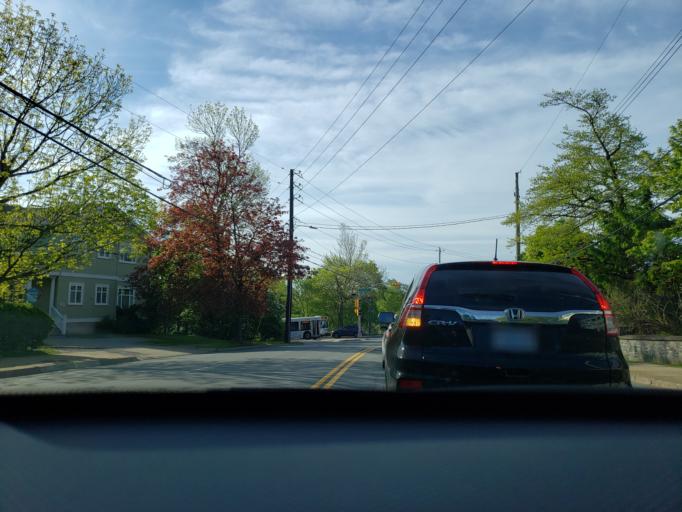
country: CA
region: Nova Scotia
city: Dartmouth
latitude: 44.6491
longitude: -63.6300
